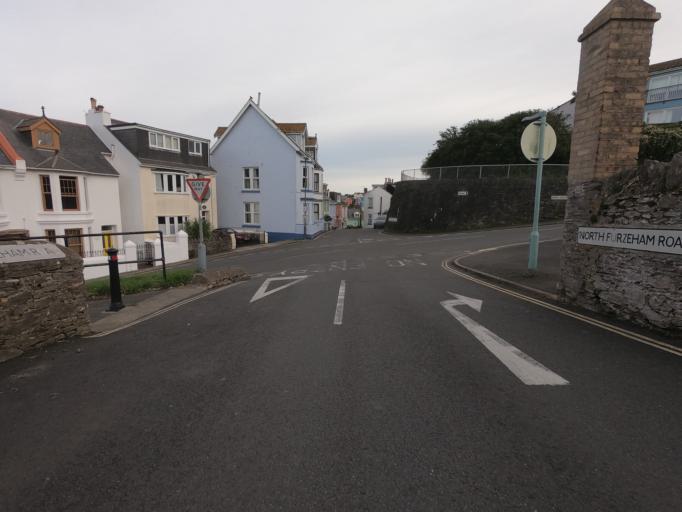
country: GB
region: England
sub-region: Borough of Torbay
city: Brixham
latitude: 50.3984
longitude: -3.5148
